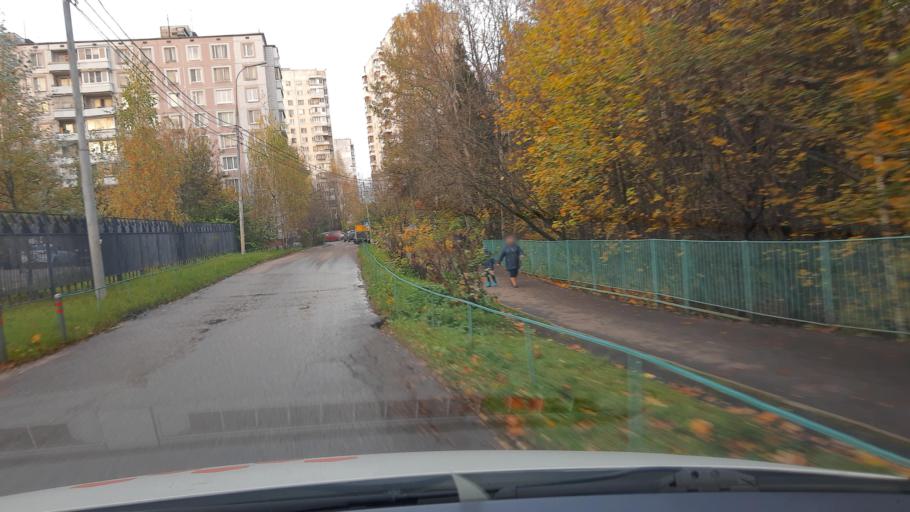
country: RU
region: Moscow
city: Yasenevo
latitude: 55.6032
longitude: 37.5547
